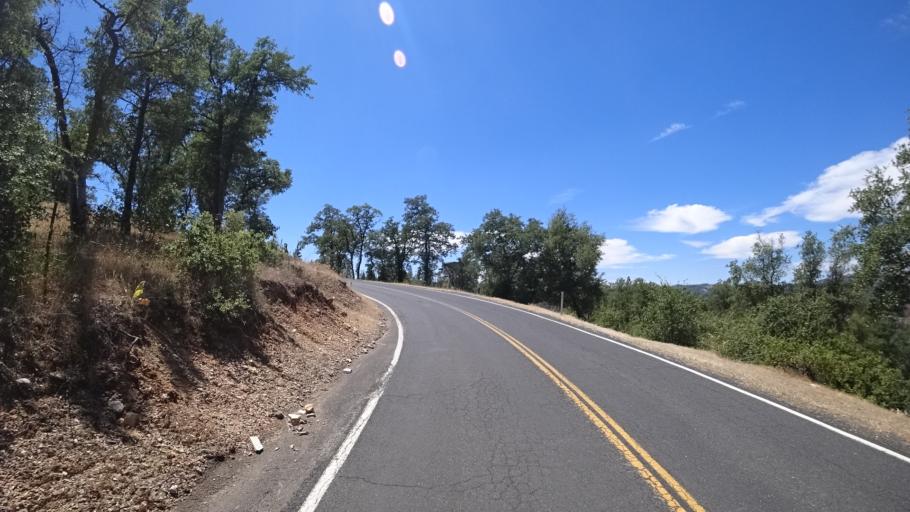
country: US
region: California
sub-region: Calaveras County
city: Forest Meadows
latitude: 38.2123
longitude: -120.4650
